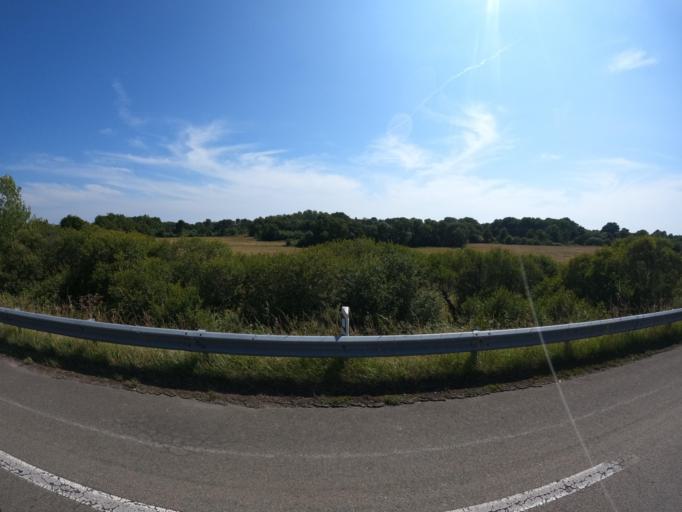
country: FR
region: Pays de la Loire
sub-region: Departement de la Loire-Atlantique
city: La Bernerie-en-Retz
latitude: 47.1049
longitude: -2.0507
